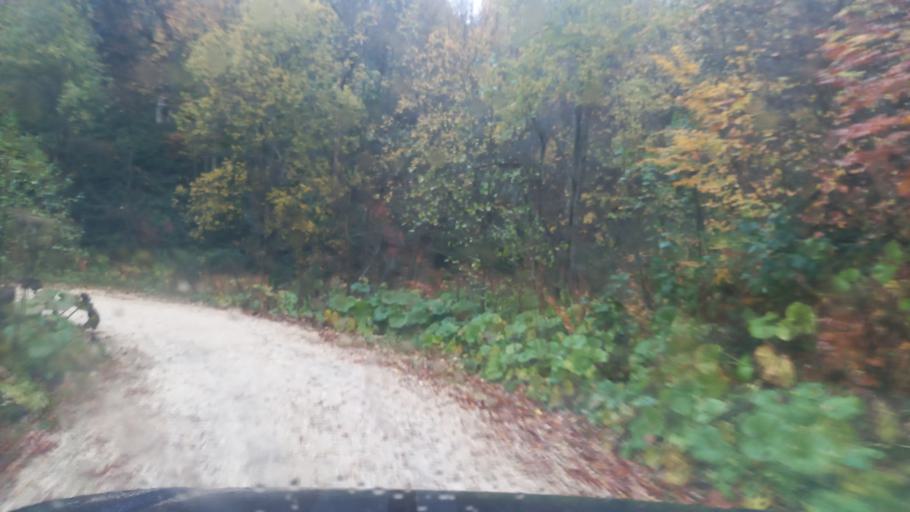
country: RU
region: Krasnodarskiy
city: Neftegorsk
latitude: 44.0184
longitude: 39.8448
